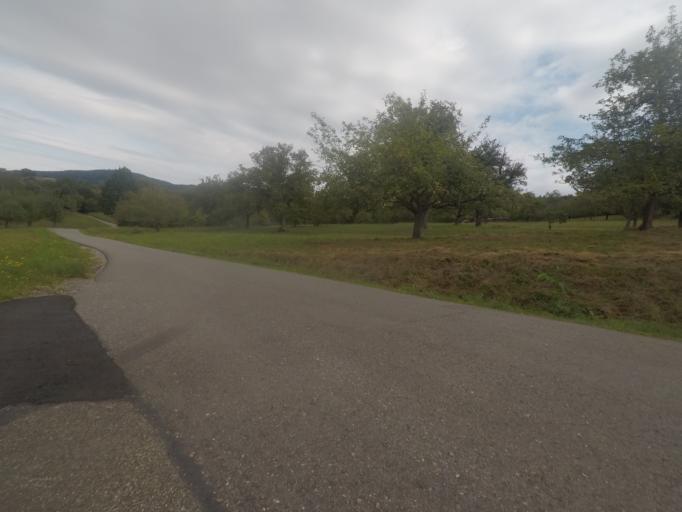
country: DE
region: Baden-Wuerttemberg
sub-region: Karlsruhe Region
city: Gaggenau
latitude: 48.8081
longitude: 8.3570
